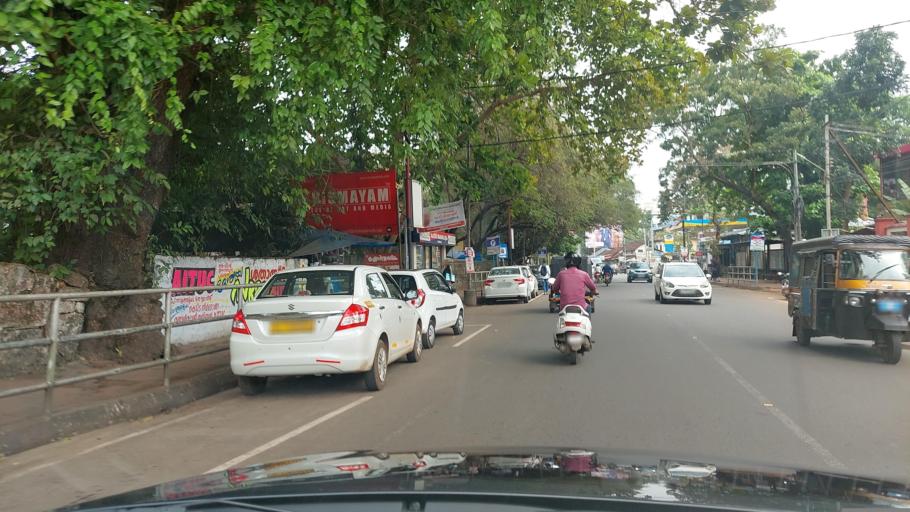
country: IN
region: Kerala
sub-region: Kozhikode
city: Kozhikode
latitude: 11.2547
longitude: 75.7826
